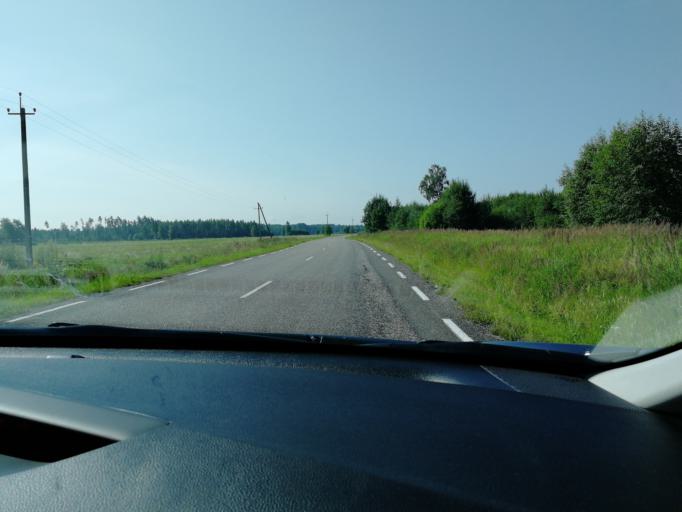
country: EE
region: Paernumaa
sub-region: Saarde vald
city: Kilingi-Nomme
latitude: 58.0281
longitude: 25.0102
